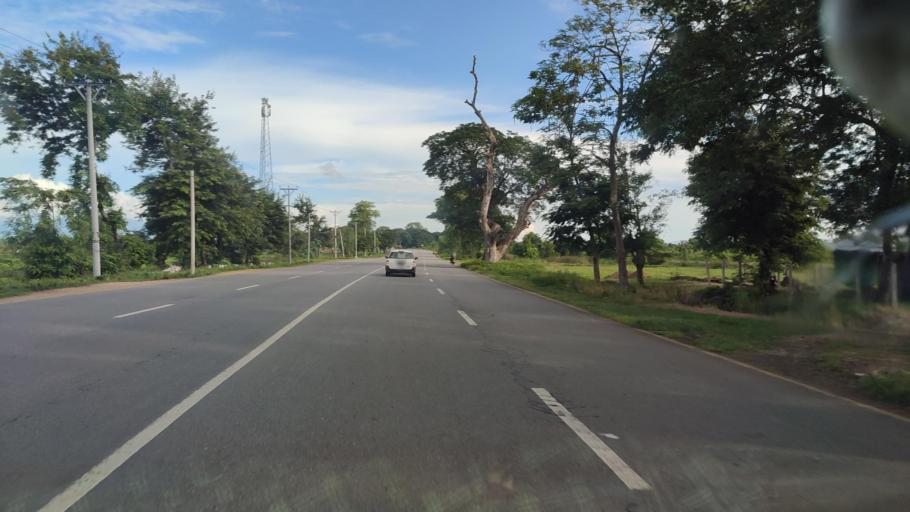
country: MM
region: Mandalay
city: Yamethin
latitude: 20.1966
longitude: 96.1830
